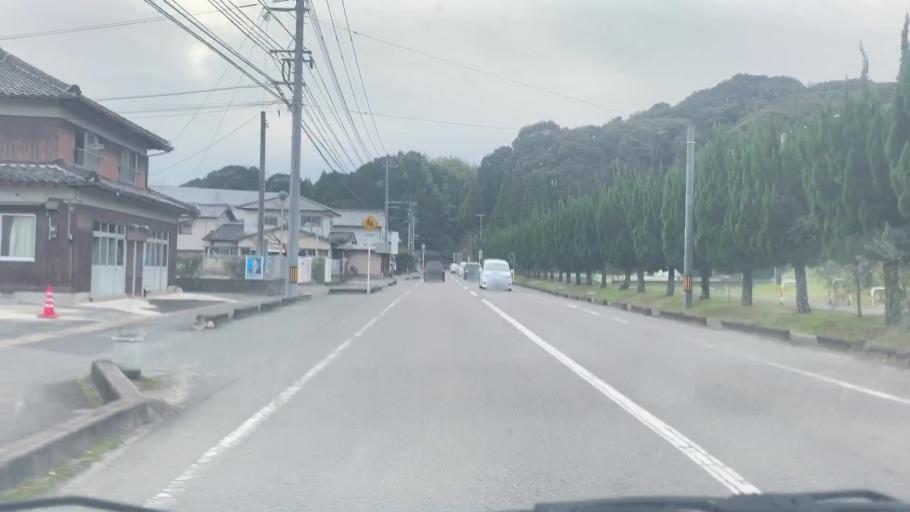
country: JP
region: Saga Prefecture
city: Takeocho-takeo
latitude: 33.1929
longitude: 130.0311
